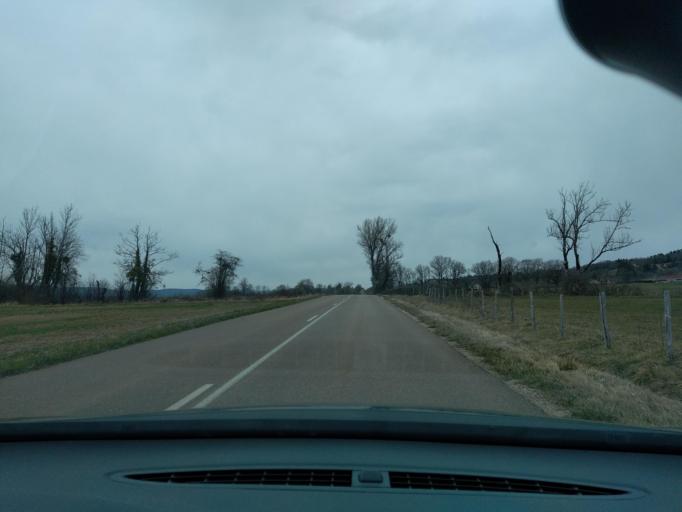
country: FR
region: Franche-Comte
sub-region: Departement du Jura
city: Arinthod
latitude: 46.3728
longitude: 5.5619
